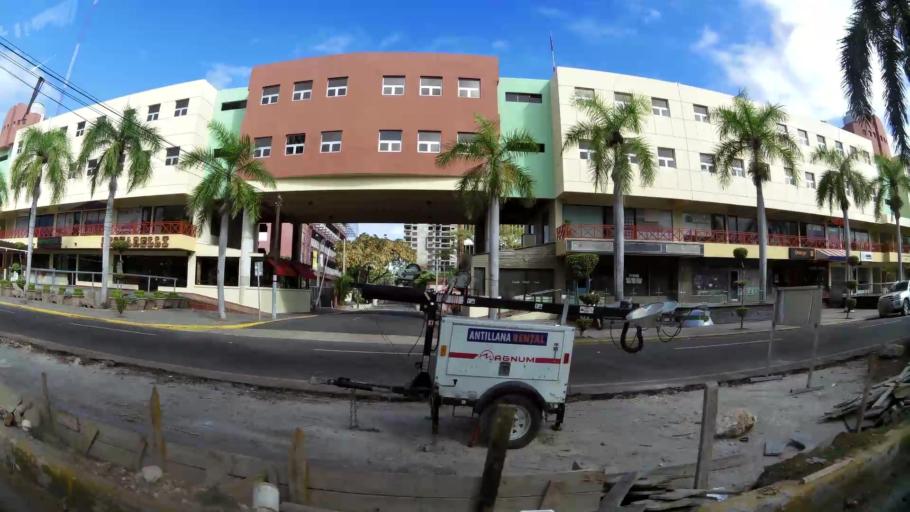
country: DO
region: Nacional
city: La Julia
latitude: 18.4593
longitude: -69.9318
